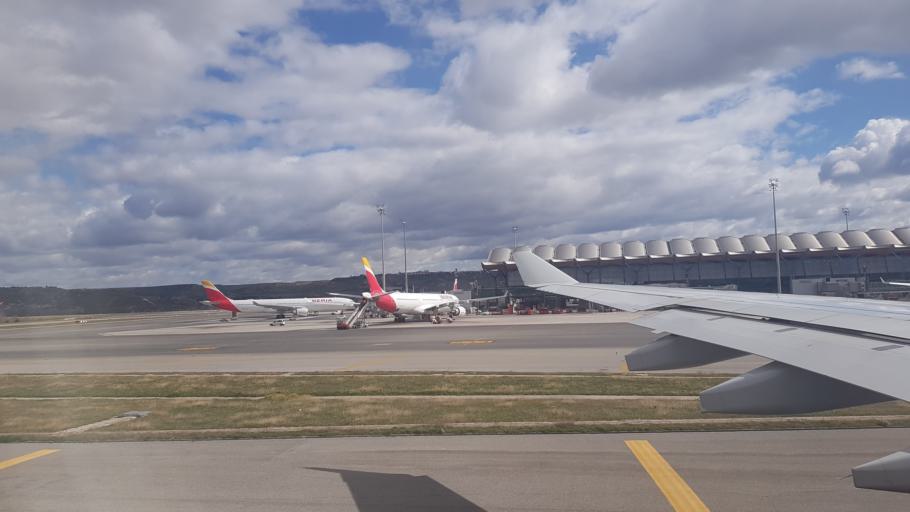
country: ES
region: Madrid
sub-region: Provincia de Madrid
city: Barajas de Madrid
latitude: 40.4983
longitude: -3.5712
